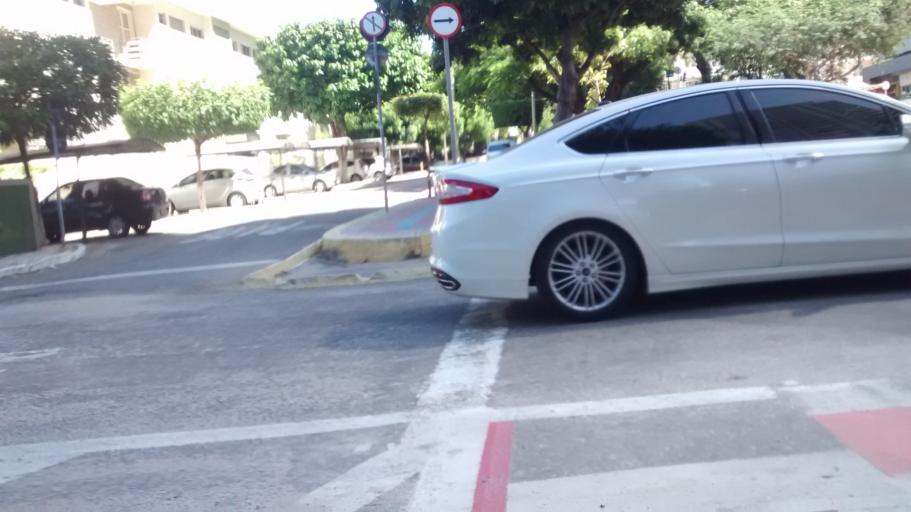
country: BR
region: Ceara
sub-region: Fortaleza
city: Fortaleza
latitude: -3.7443
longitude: -38.5032
